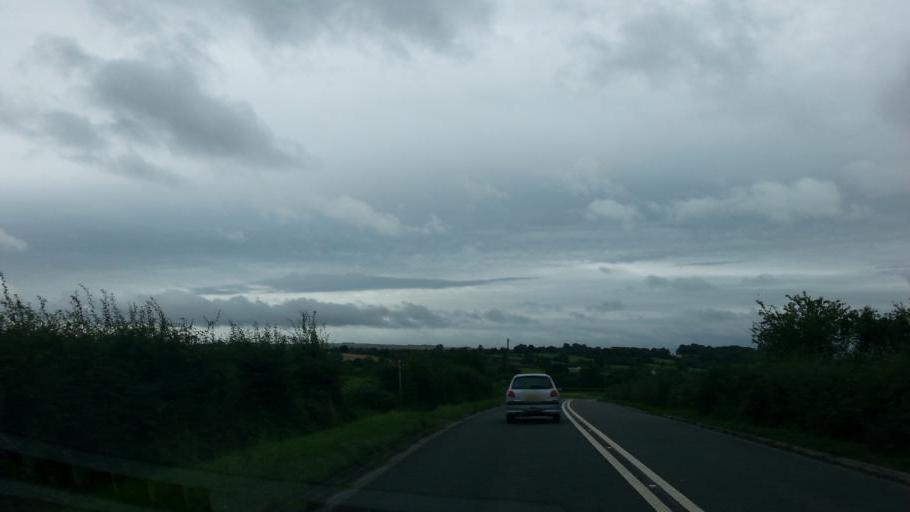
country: GB
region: England
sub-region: Wiltshire
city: Melksham
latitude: 51.3301
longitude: -2.1502
